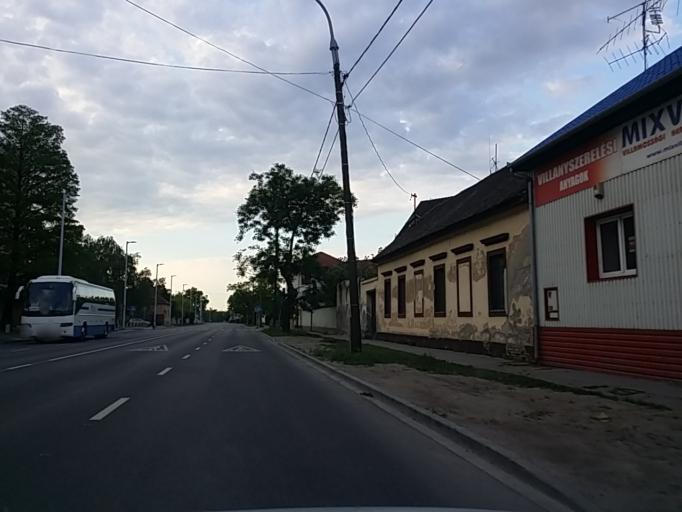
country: HU
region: Bacs-Kiskun
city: Kecskemet
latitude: 46.9071
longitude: 19.7033
